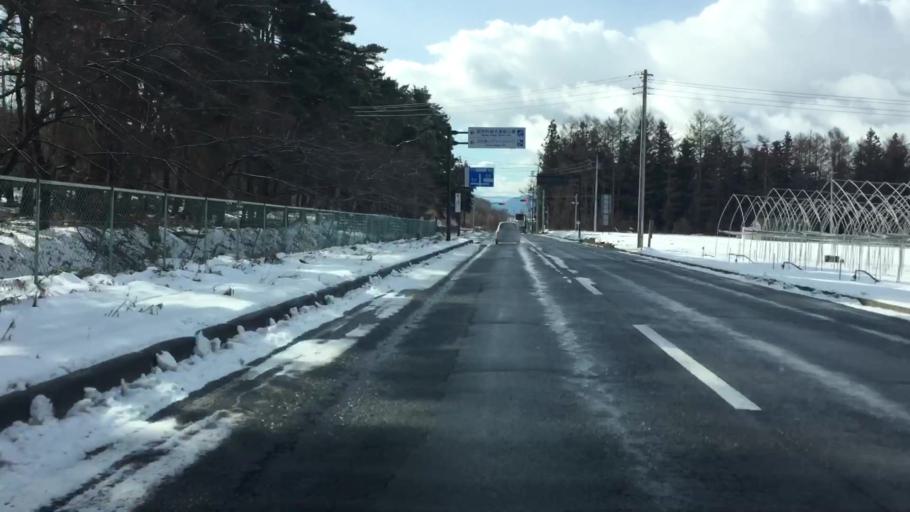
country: JP
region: Gunma
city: Numata
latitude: 36.6237
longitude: 139.0896
